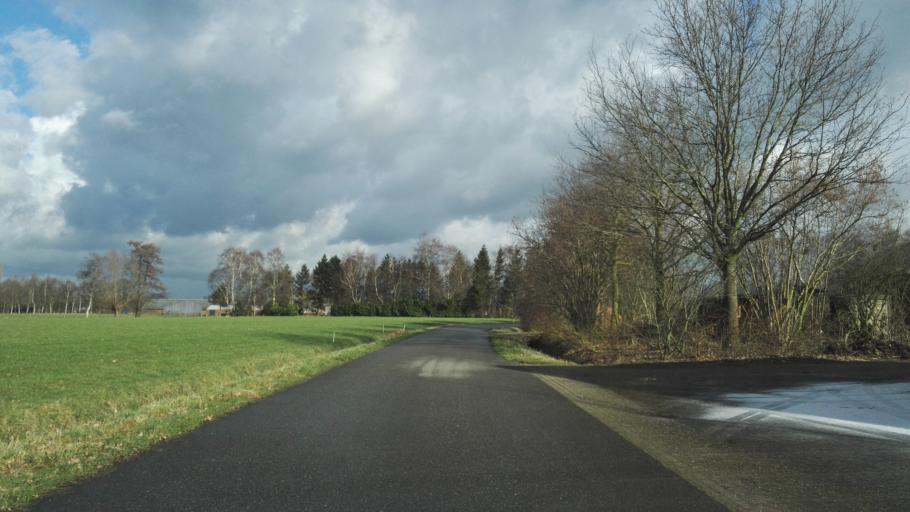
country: NL
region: Gelderland
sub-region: Gemeente Apeldoorn
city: Apeldoorn
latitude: 52.2405
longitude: 6.0176
